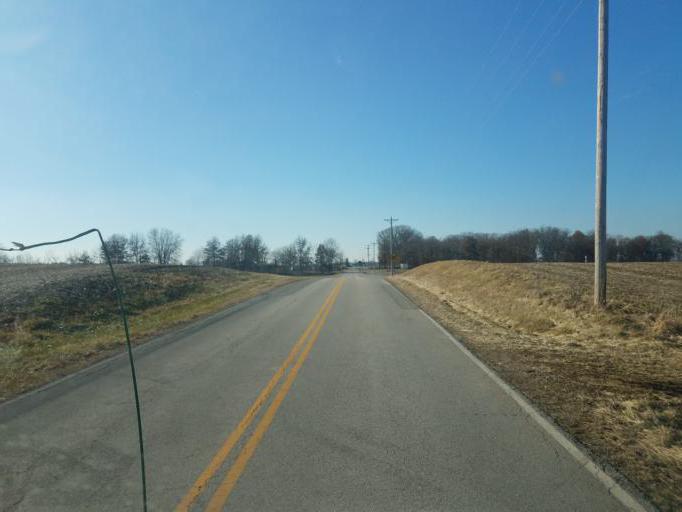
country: US
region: Ohio
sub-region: Marion County
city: Marion
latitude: 40.6442
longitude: -83.1779
